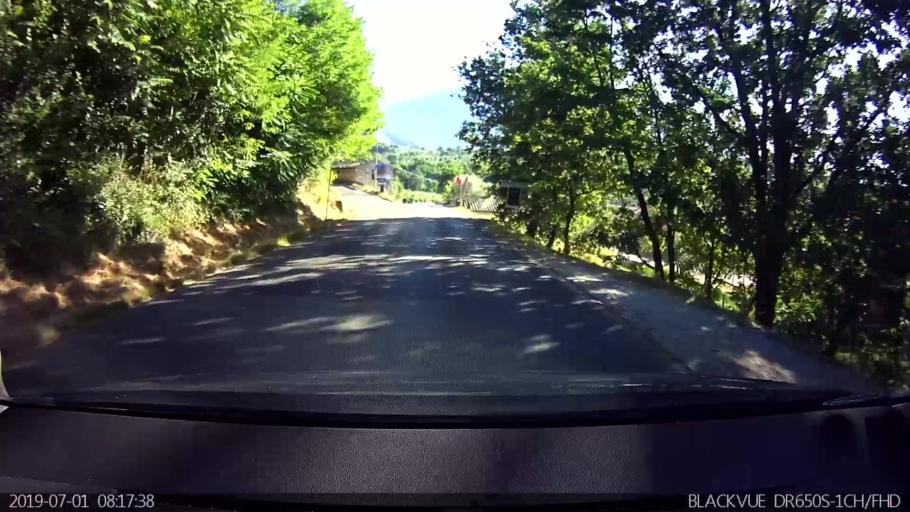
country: IT
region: Latium
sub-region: Provincia di Frosinone
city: Veroli
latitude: 41.7077
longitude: 13.4398
